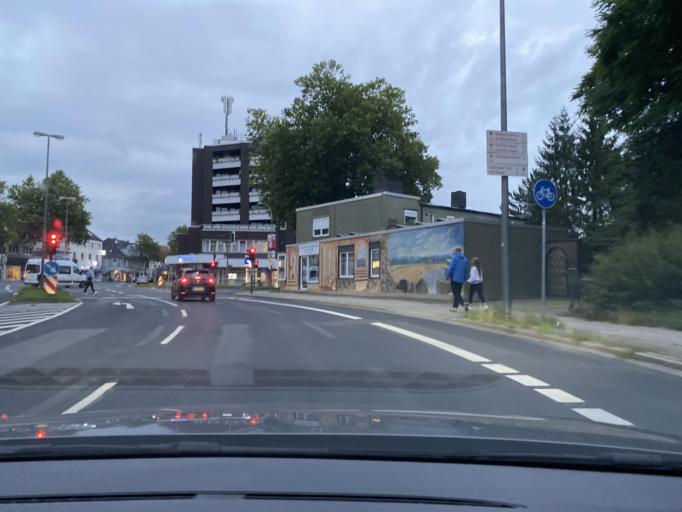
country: DE
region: North Rhine-Westphalia
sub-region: Regierungsbezirk Arnsberg
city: Bochum
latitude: 51.4399
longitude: 7.2118
